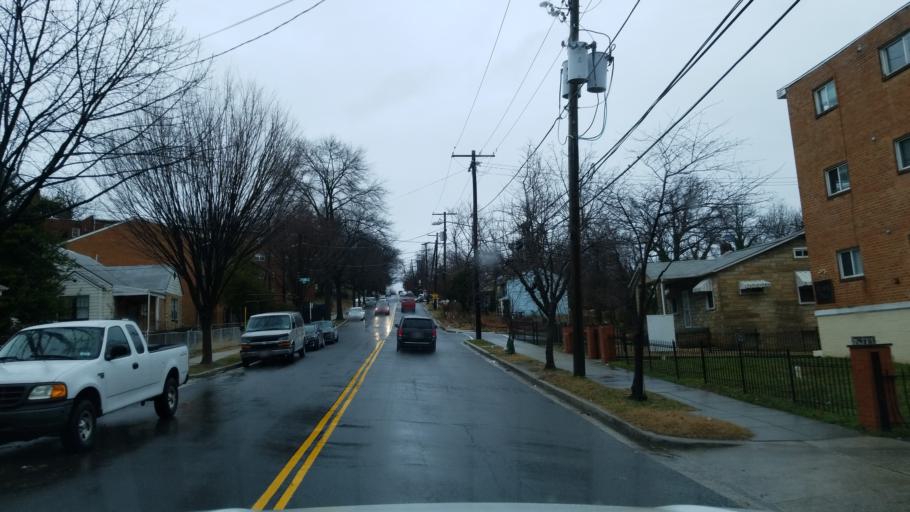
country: US
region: Maryland
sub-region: Prince George's County
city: Glassmanor
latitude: 38.8315
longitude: -77.0059
